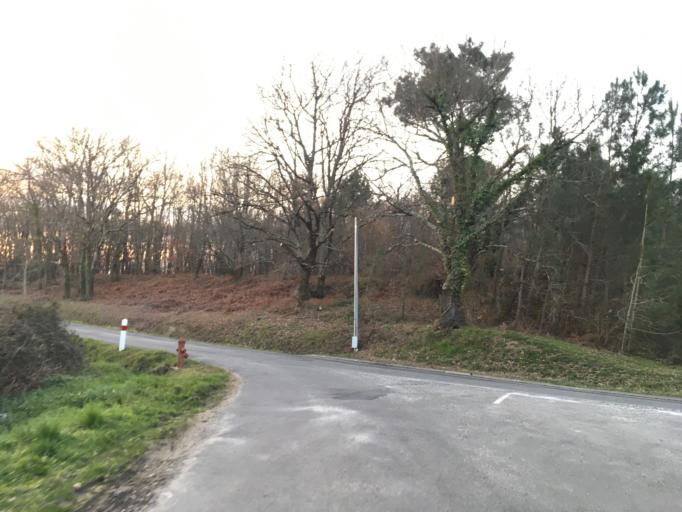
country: FR
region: Aquitaine
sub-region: Departement de la Gironde
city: Saint-Ciers-sur-Gironde
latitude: 45.3008
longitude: -0.6001
